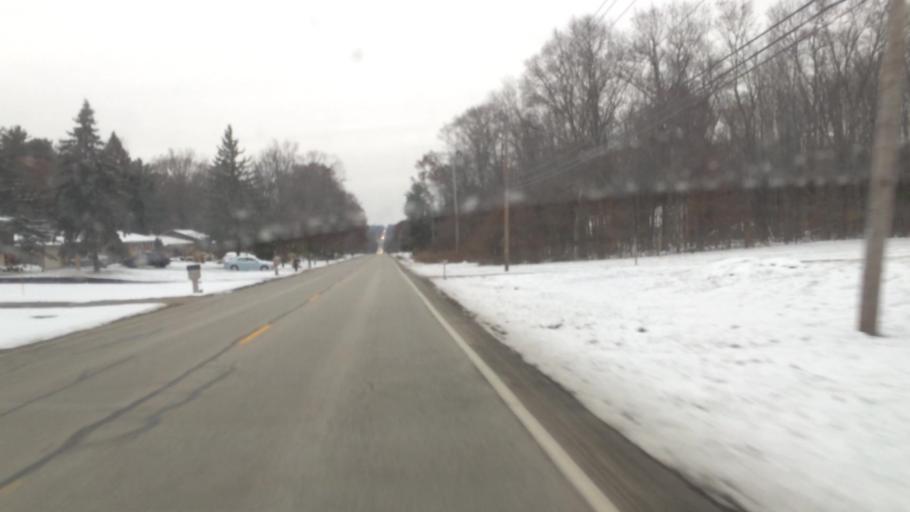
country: US
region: Ohio
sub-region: Cuyahoga County
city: Strongsville
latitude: 41.2965
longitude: -81.7852
